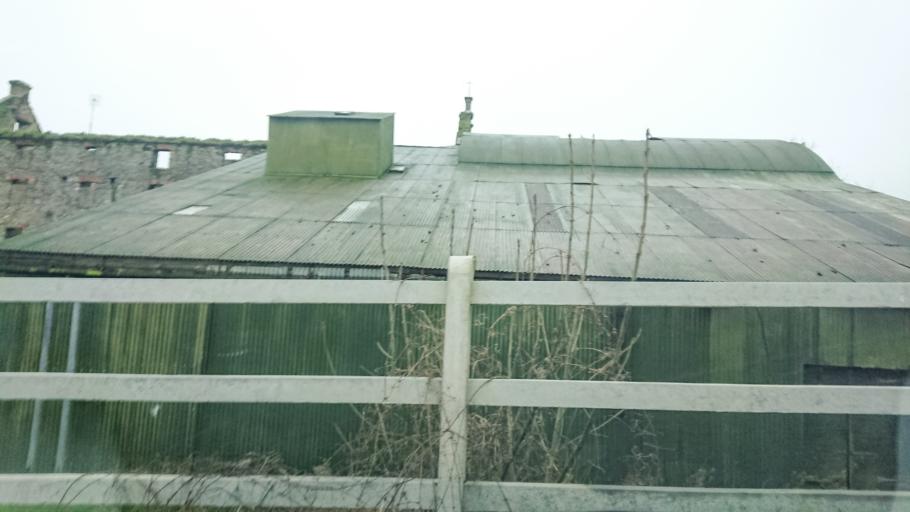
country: IE
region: Munster
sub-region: County Cork
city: Castlemartyr
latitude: 51.9431
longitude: -7.9927
